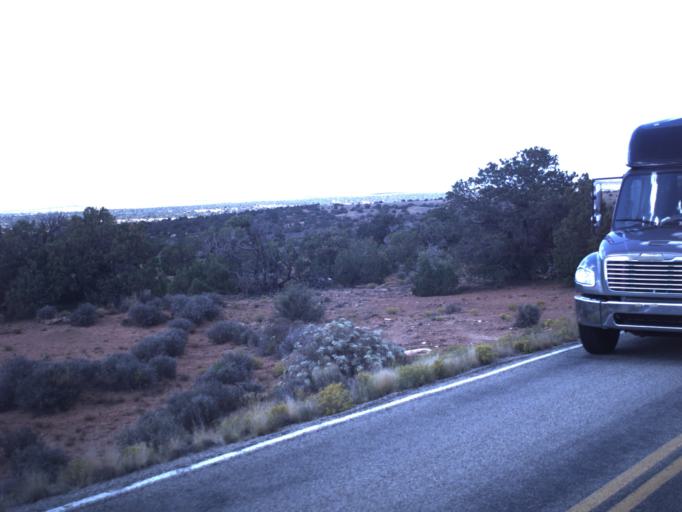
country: US
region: Utah
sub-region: Grand County
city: Moab
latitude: 38.4893
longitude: -109.7365
